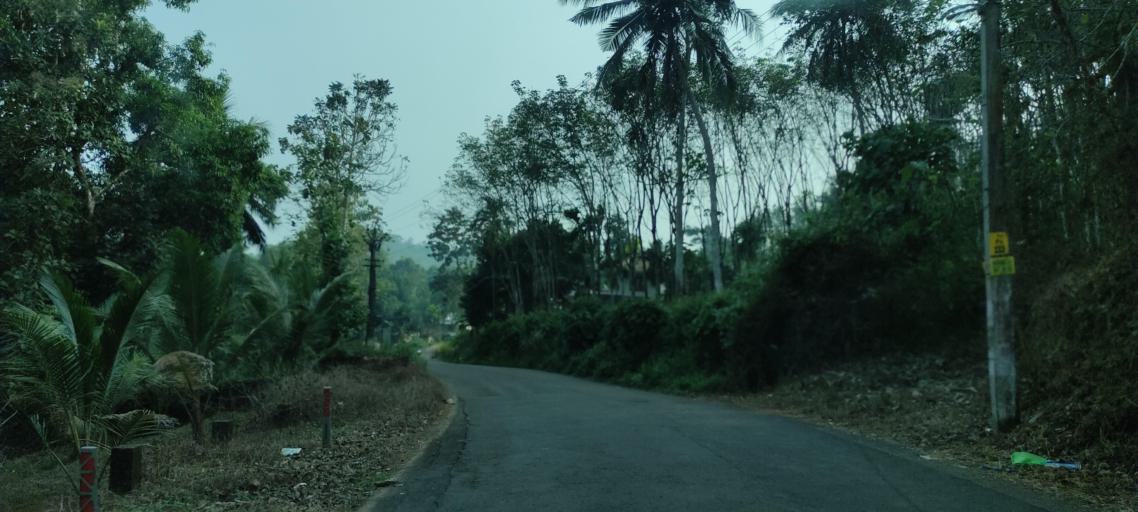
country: IN
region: Kerala
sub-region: Ernakulam
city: Piravam
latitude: 9.7945
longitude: 76.4989
